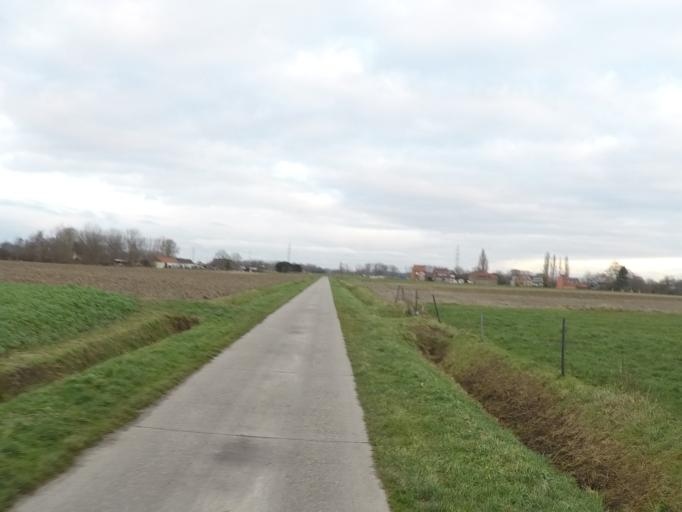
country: BE
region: Flanders
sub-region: Provincie Vlaams-Brabant
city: Merchtem
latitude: 50.9949
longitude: 4.2480
